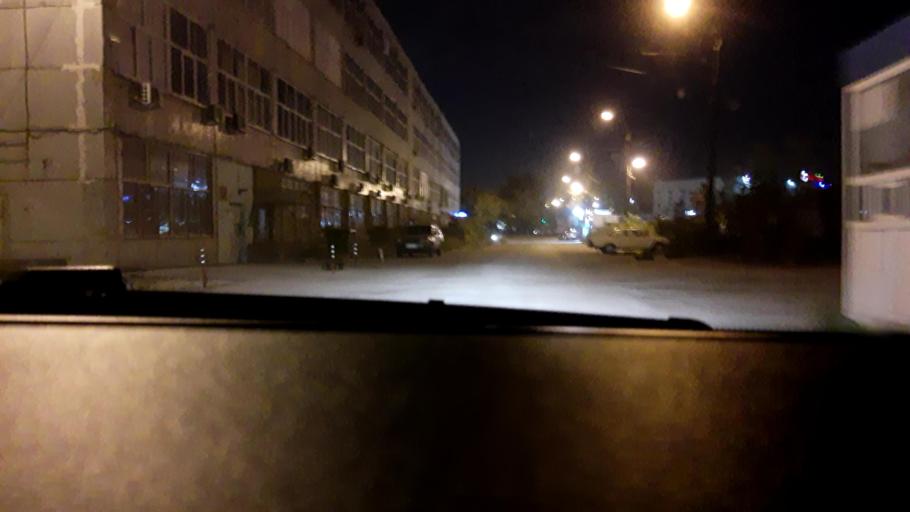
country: RU
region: Nizjnij Novgorod
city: Neklyudovo
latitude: 56.3637
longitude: 43.8602
